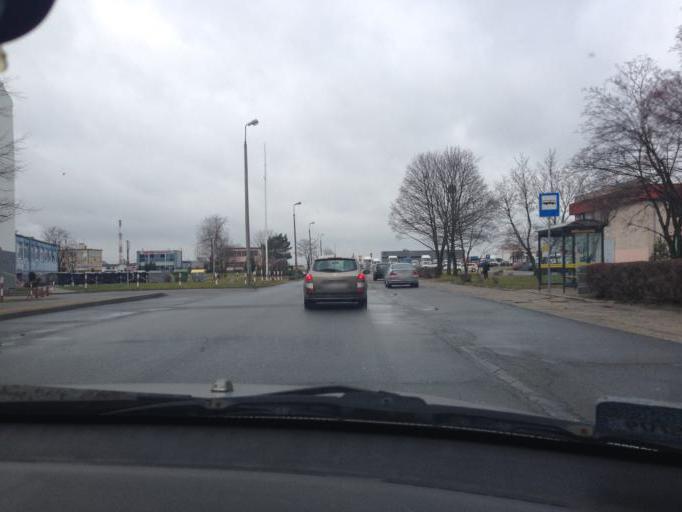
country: PL
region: Opole Voivodeship
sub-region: Powiat opolski
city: Opole
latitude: 50.6827
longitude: 17.9445
